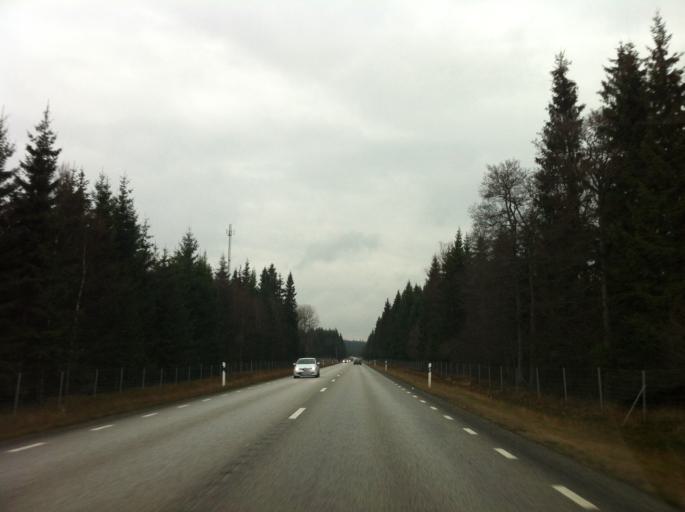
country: SE
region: Joenkoeping
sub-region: Savsjo Kommun
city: Saevsjoe
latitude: 57.3902
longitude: 14.6365
